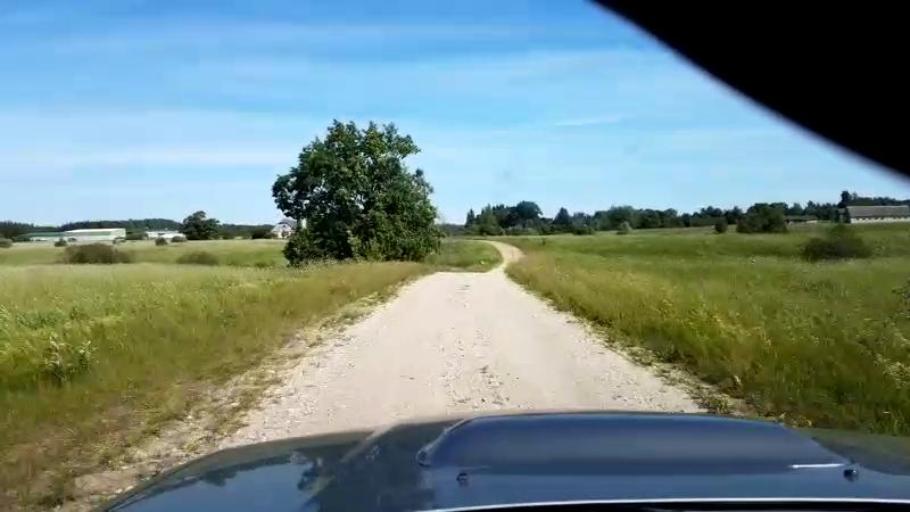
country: EE
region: Paernumaa
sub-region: Sauga vald
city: Sauga
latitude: 58.4799
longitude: 24.5309
